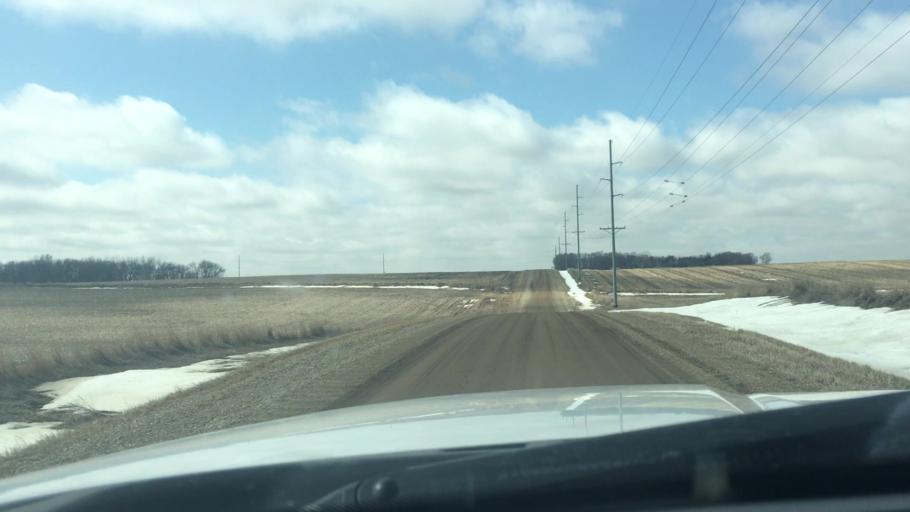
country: US
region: South Dakota
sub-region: Minnehaha County
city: Crooks
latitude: 43.6164
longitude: -96.8037
